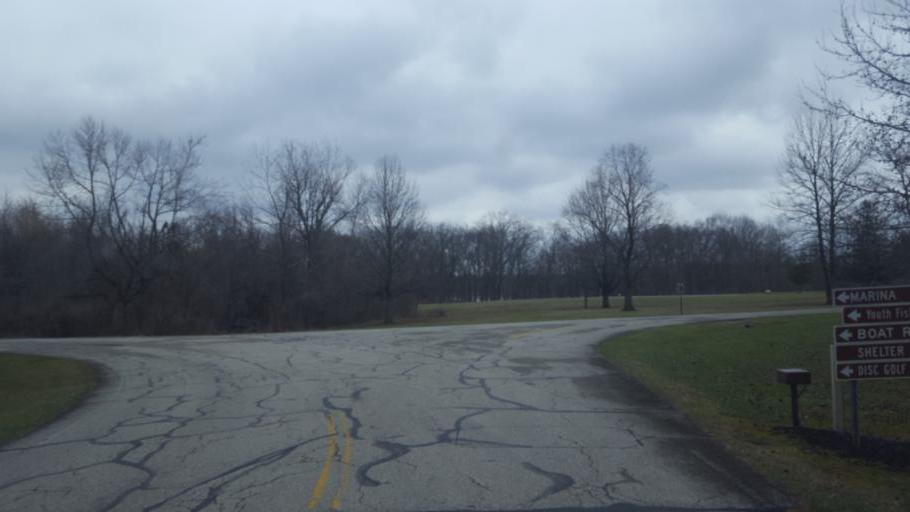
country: US
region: Ohio
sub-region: Delaware County
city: Delaware
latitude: 40.3787
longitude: -83.0611
